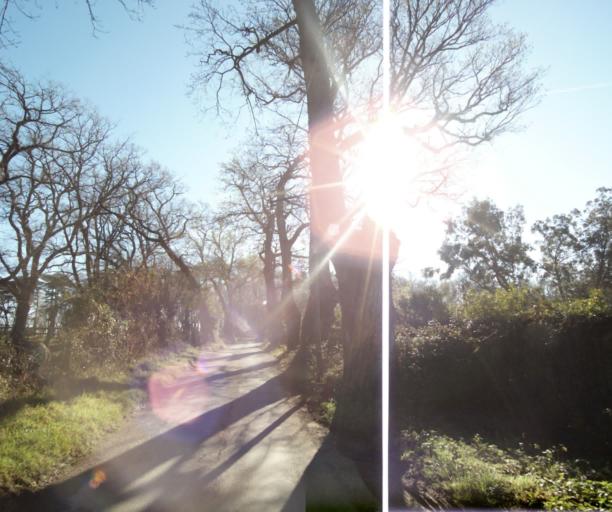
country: FR
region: Aquitaine
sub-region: Departement des Pyrenees-Atlantiques
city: Ciboure
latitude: 43.3690
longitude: -1.6681
